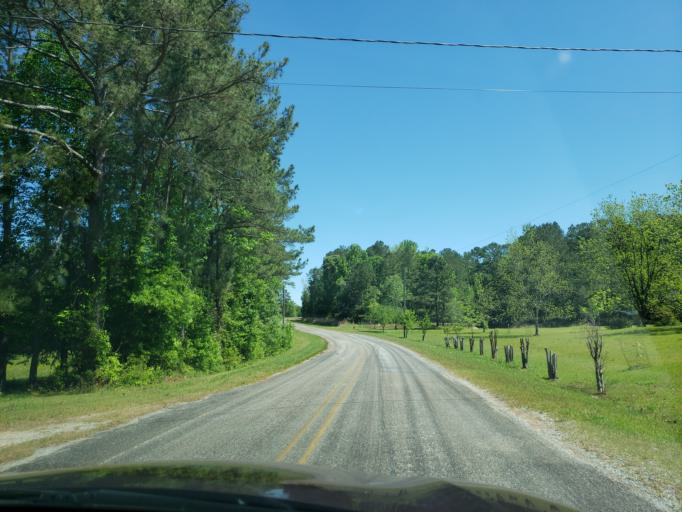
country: US
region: Alabama
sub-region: Elmore County
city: Eclectic
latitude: 32.6987
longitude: -85.8885
